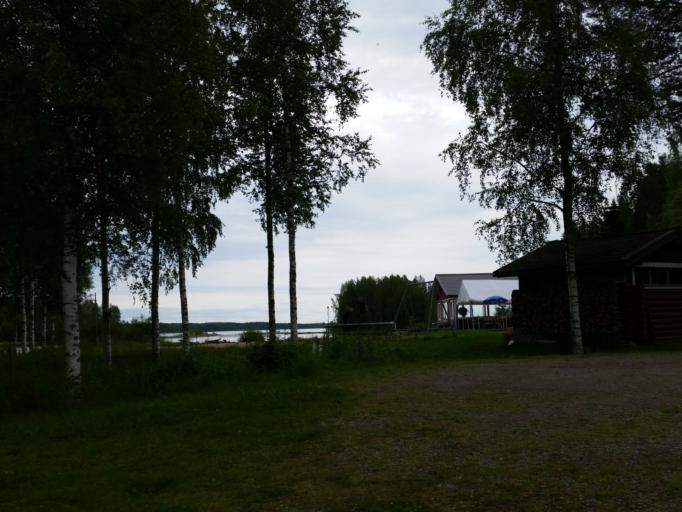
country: FI
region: Northern Savo
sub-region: Sisae-Savo
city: Tervo
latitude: 63.0063
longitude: 26.6885
